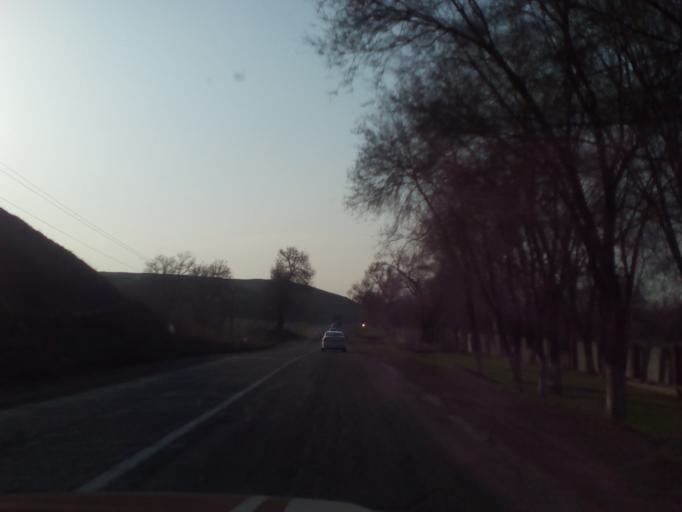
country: KZ
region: Almaty Oblysy
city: Burunday
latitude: 43.1693
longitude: 76.5384
